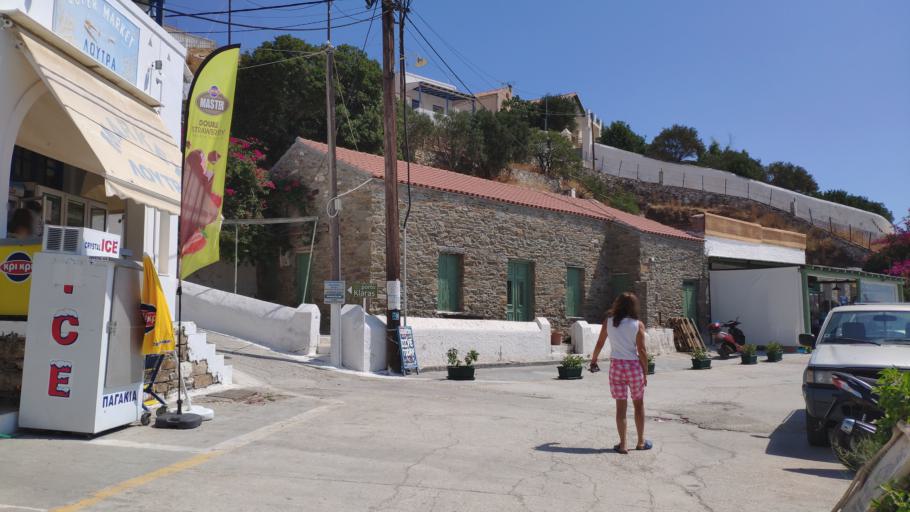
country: GR
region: South Aegean
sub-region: Nomos Kykladon
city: Kythnos
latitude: 37.4431
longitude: 24.4253
